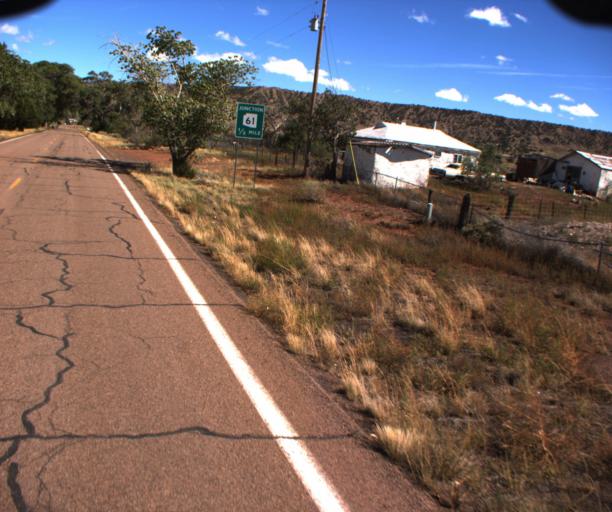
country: US
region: Arizona
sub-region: Apache County
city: Saint Johns
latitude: 34.4781
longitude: -109.6099
